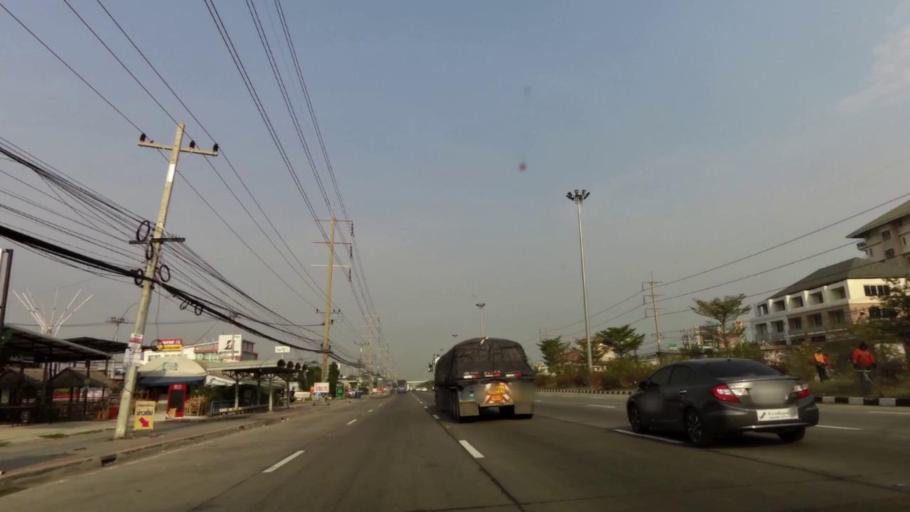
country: TH
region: Phra Nakhon Si Ayutthaya
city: Phra Nakhon Si Ayutthaya
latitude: 14.3262
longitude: 100.6272
